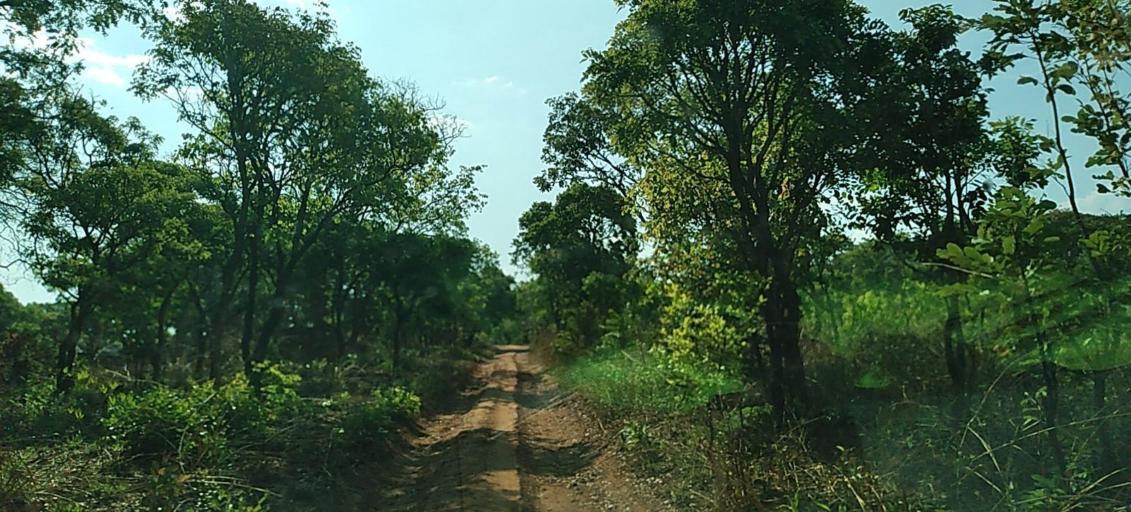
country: ZM
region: North-Western
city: Mwinilunga
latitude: -11.2998
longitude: 24.8700
